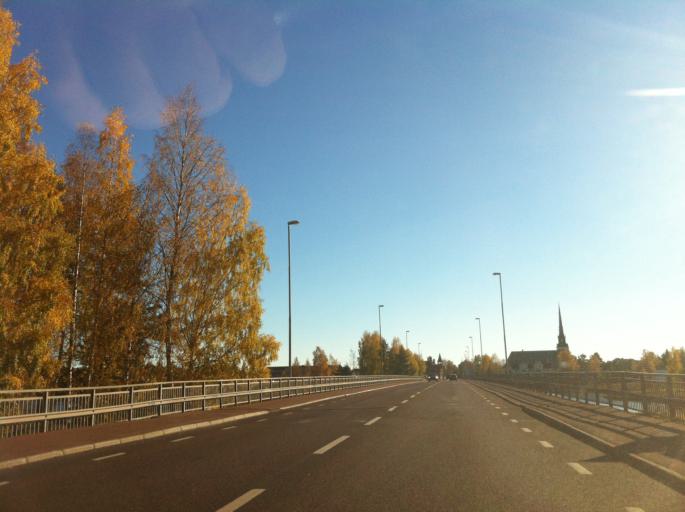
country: SE
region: Dalarna
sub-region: Mora Kommun
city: Mora
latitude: 61.0136
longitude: 14.5396
